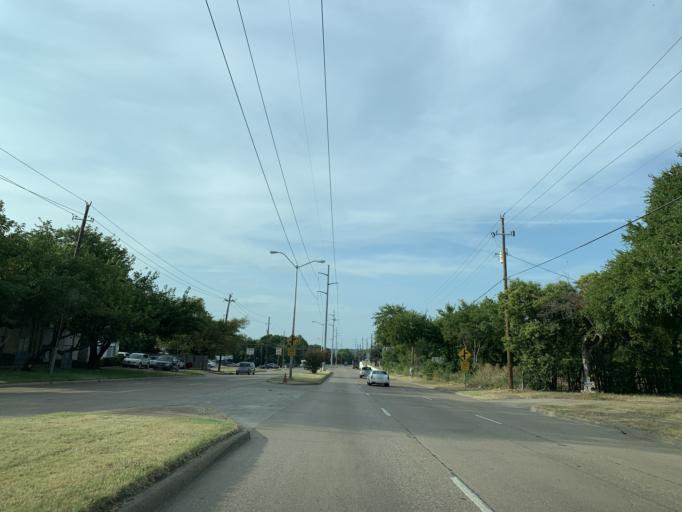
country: US
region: Texas
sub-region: Dallas County
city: Cockrell Hill
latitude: 32.6937
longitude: -96.8914
